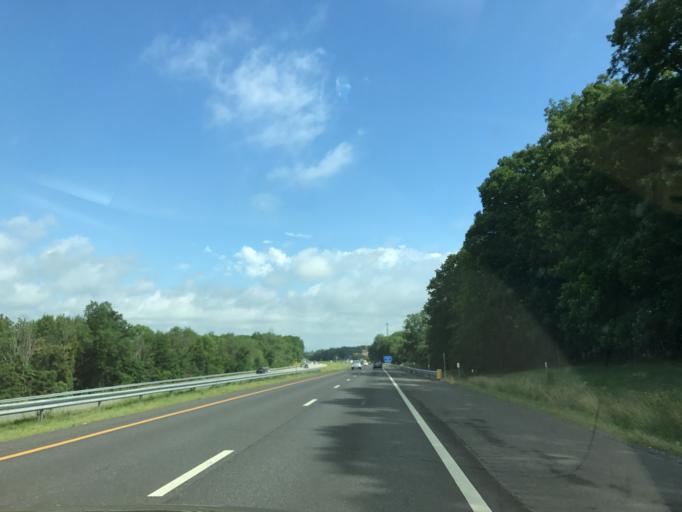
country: US
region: New York
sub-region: Orange County
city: Orange Lake
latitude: 41.5700
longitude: -74.0839
